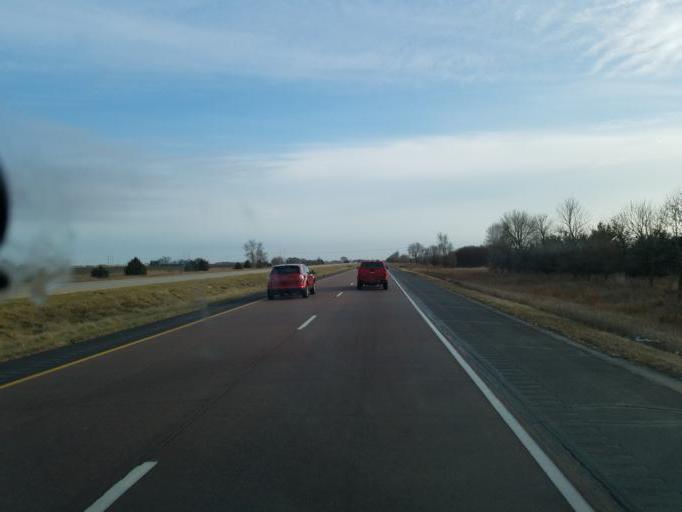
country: US
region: Iowa
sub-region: Woodbury County
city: Sergeant Bluff
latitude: 42.3652
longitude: -96.3465
